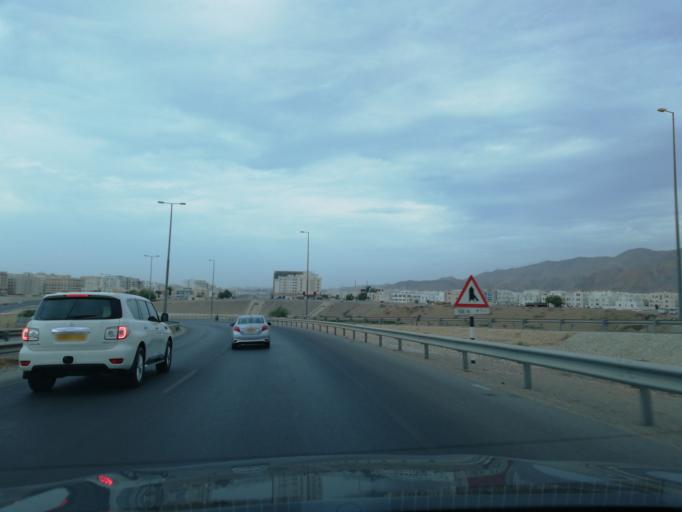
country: OM
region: Muhafazat Masqat
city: Bawshar
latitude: 23.5815
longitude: 58.4179
